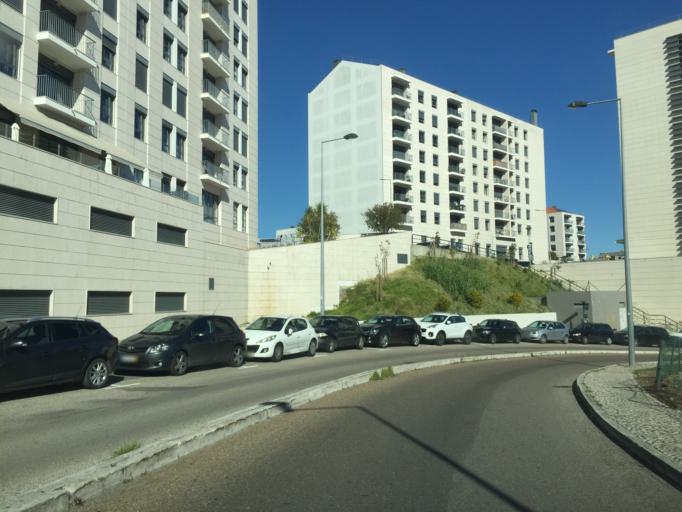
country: PT
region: Lisbon
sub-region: Odivelas
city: Olival do Basto
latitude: 38.7631
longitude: -9.1636
